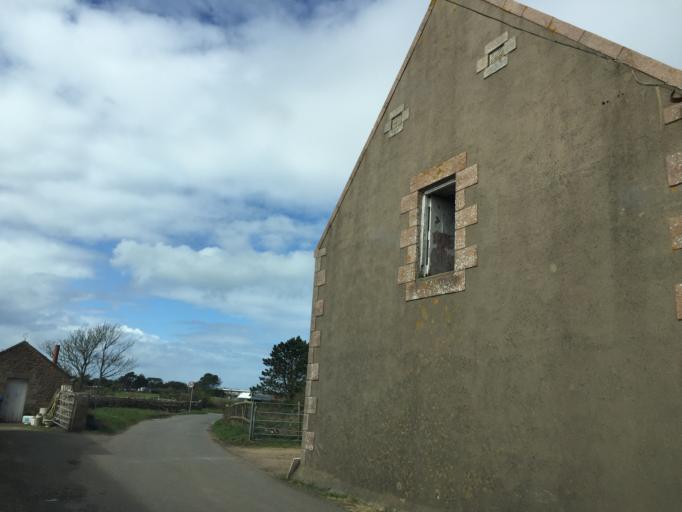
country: JE
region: St Helier
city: Saint Helier
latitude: 49.1744
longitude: -2.1716
